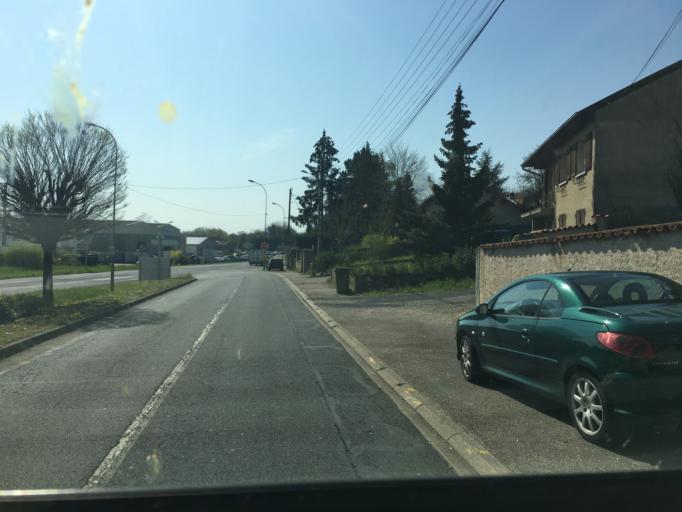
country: FR
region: Lorraine
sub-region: Departement de Meurthe-et-Moselle
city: Norroy-les-Pont-a-Mousson
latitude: 48.9314
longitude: 6.0373
